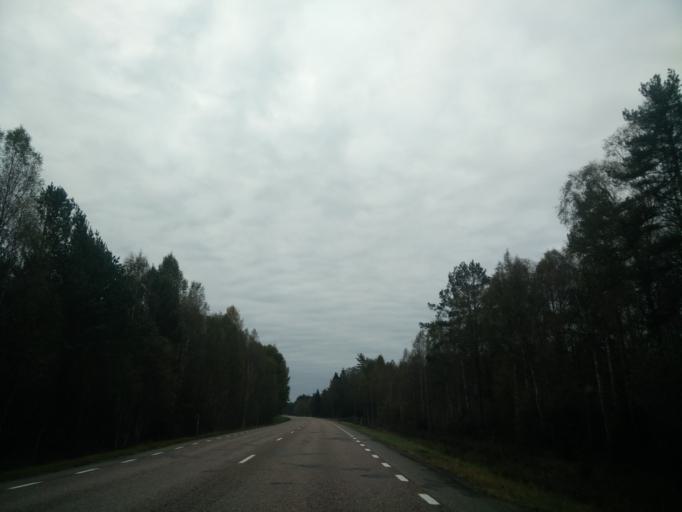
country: SE
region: Gaevleborg
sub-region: Gavle Kommun
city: Norrsundet
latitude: 60.8559
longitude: 17.1869
